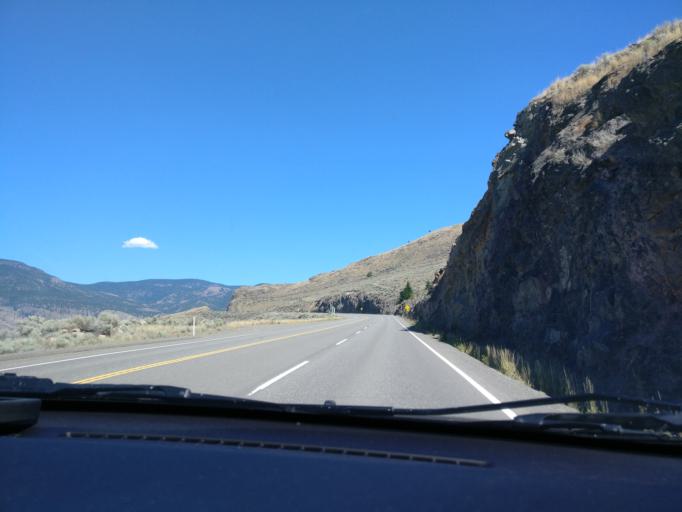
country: CA
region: British Columbia
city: Logan Lake
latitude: 50.7644
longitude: -120.7826
